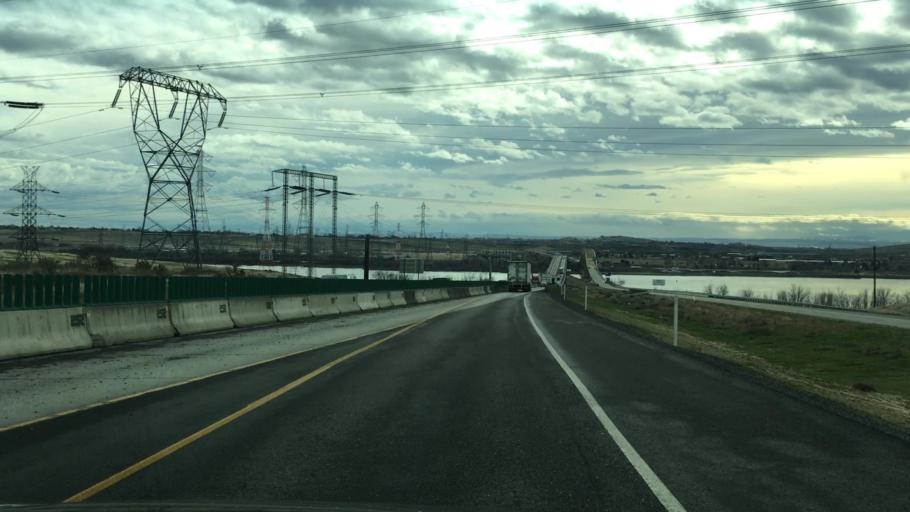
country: US
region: Oregon
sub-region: Umatilla County
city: Umatilla
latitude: 45.9406
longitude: -119.3321
